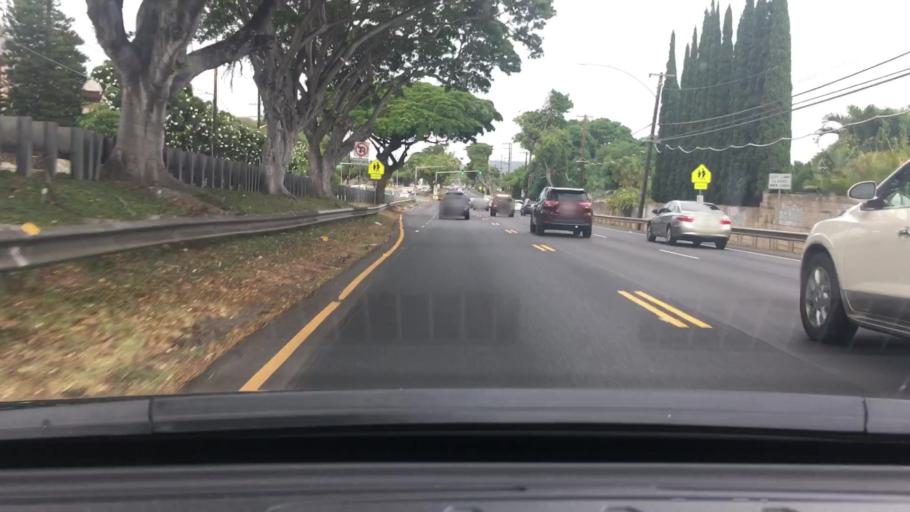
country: US
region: Hawaii
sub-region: Honolulu County
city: Honolulu
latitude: 21.2776
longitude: -157.7779
